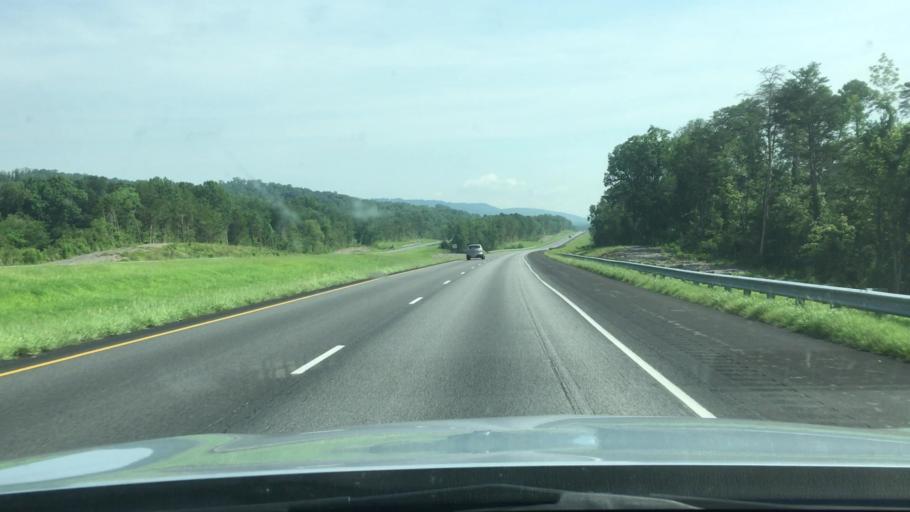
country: US
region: Georgia
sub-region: Dade County
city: Trenton
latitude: 34.8372
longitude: -85.5337
